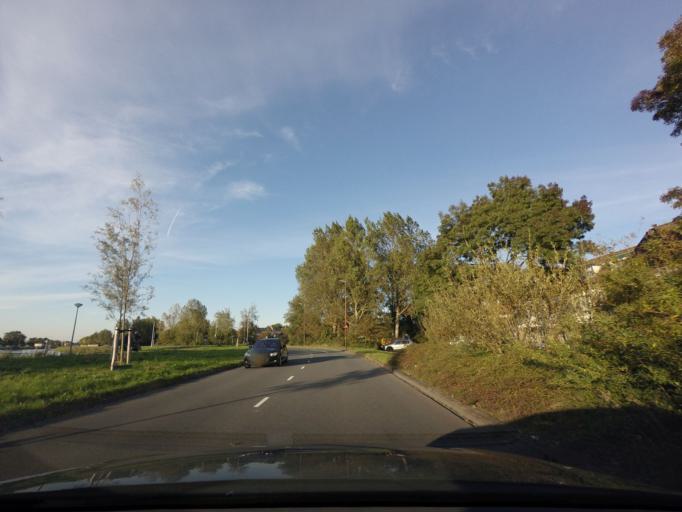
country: NL
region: North Holland
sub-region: Gemeente Alkmaar
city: Alkmaar
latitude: 52.6573
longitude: 4.7469
